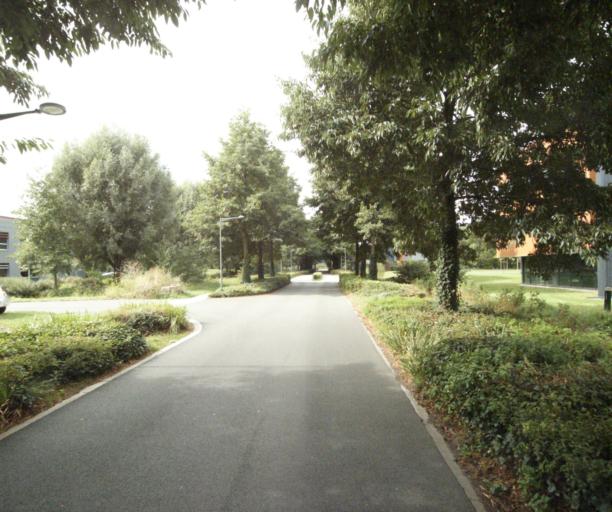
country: FR
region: Nord-Pas-de-Calais
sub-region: Departement du Nord
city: Villeneuve-d'Ascq
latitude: 50.6039
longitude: 3.1524
